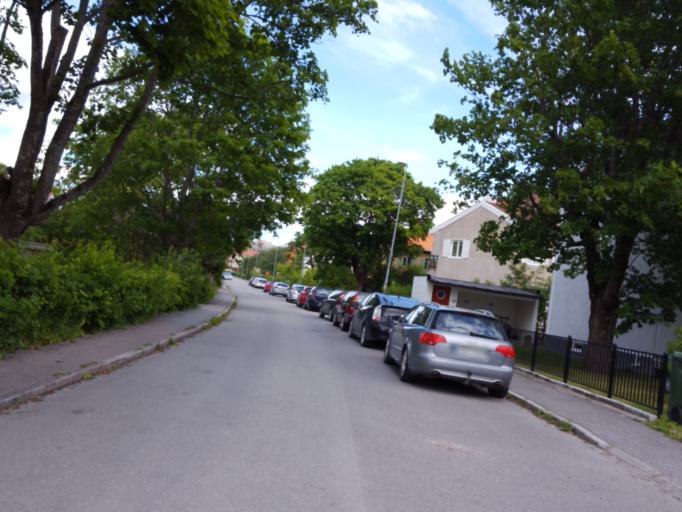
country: SE
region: Uppsala
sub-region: Uppsala Kommun
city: Uppsala
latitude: 59.8445
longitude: 17.6295
